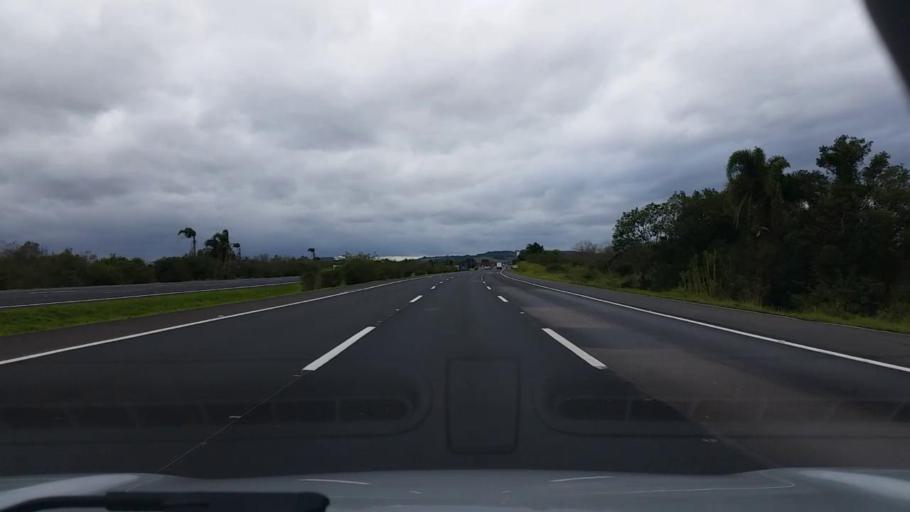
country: BR
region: Rio Grande do Sul
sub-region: Osorio
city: Osorio
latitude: -29.8817
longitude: -50.4365
